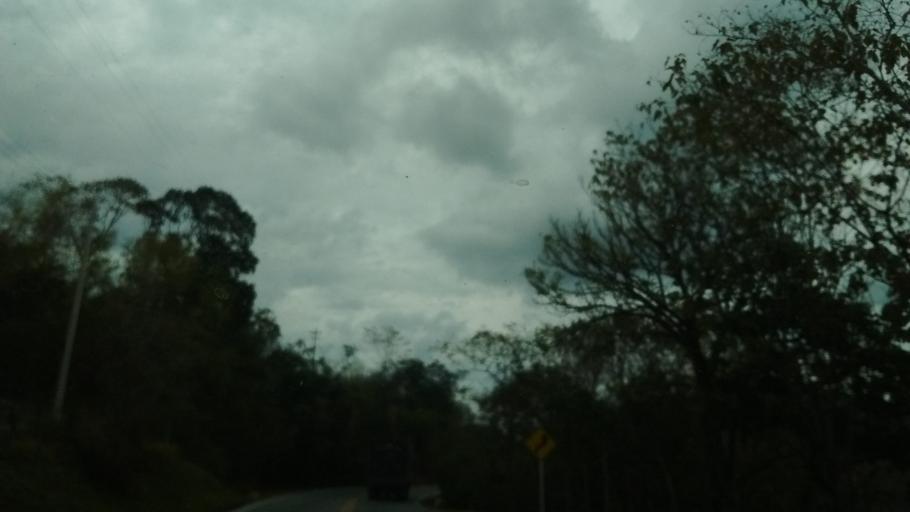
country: CO
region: Cauca
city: Rosas
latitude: 2.2734
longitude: -76.7249
